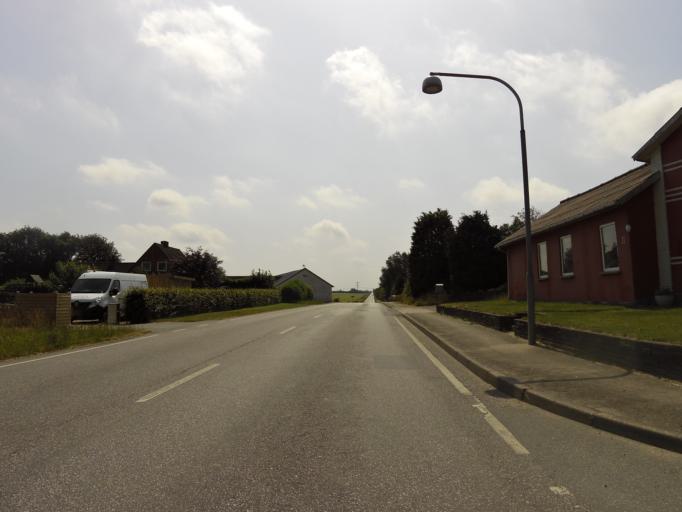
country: DK
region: South Denmark
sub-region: Aabenraa Kommune
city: Rodekro
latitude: 55.1430
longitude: 9.2046
